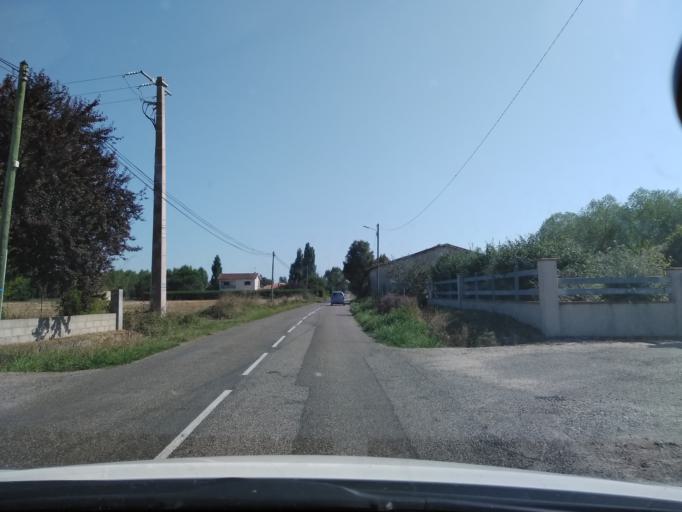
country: FR
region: Midi-Pyrenees
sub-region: Departement du Tarn-et-Garonne
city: Montech
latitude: 43.9665
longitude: 1.2376
